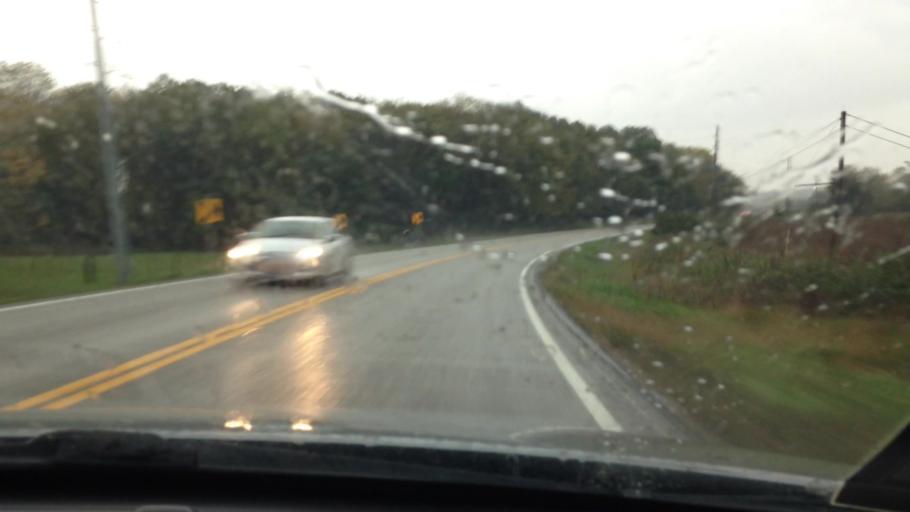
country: US
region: Missouri
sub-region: Platte County
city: Platte City
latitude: 39.3822
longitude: -94.8056
